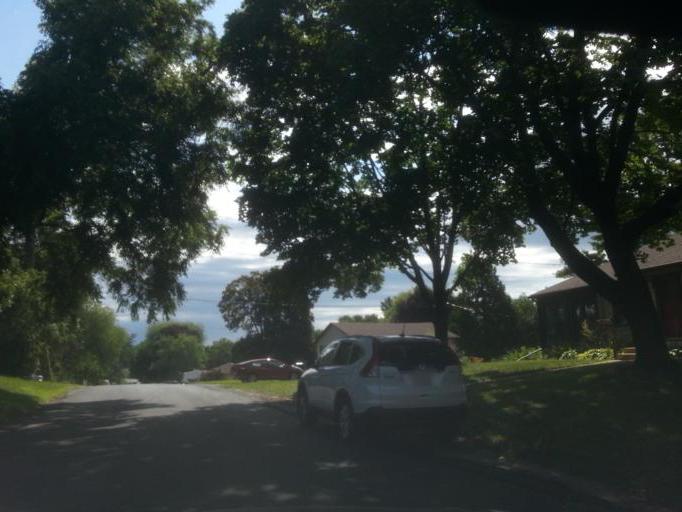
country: US
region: Wisconsin
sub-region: Dane County
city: Monona
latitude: 43.1090
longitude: -89.3305
